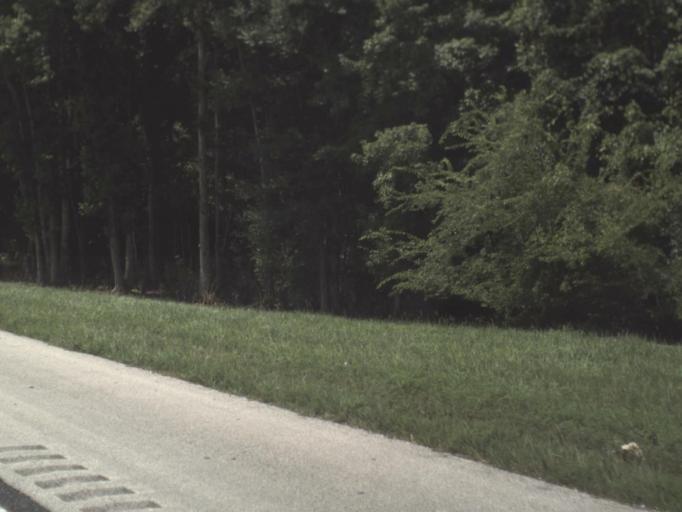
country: US
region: Florida
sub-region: Saint Johns County
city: Villano Beach
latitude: 29.9641
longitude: -81.4487
